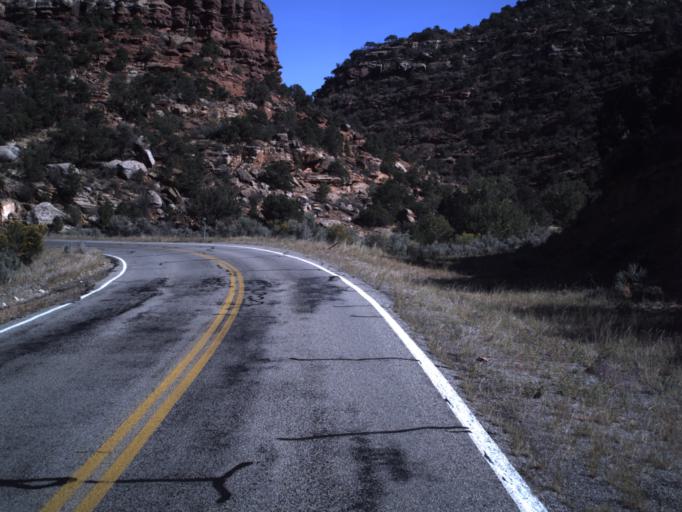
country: US
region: Utah
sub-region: San Juan County
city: Monticello
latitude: 37.9827
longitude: -109.5037
